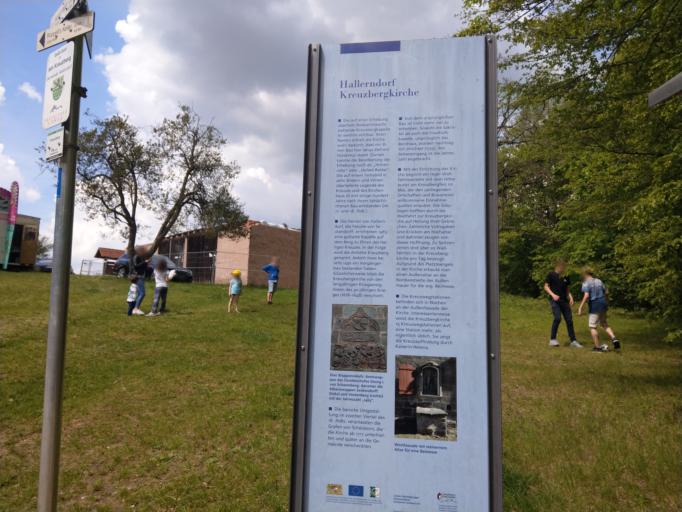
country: DE
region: Bavaria
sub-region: Upper Franconia
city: Hallerndorf
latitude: 49.7594
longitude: 10.9553
